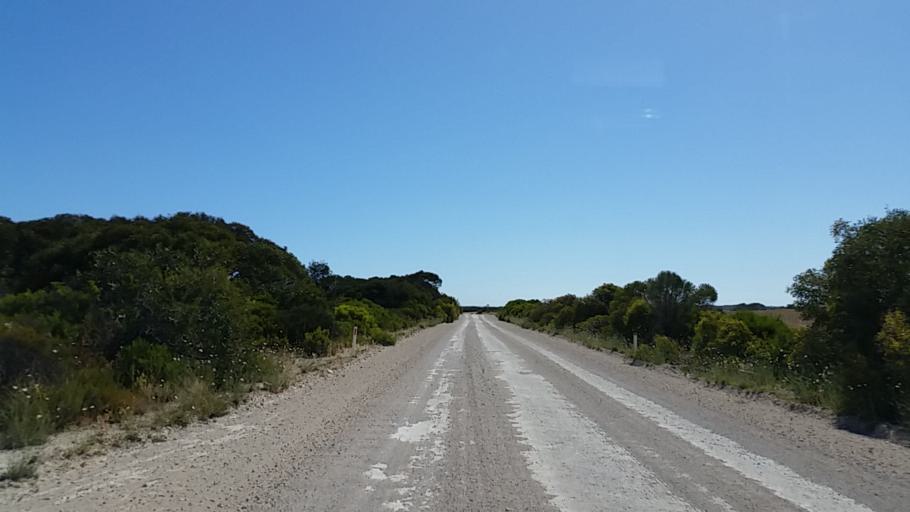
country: AU
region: South Australia
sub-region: Yorke Peninsula
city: Honiton
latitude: -35.2202
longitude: 137.0792
